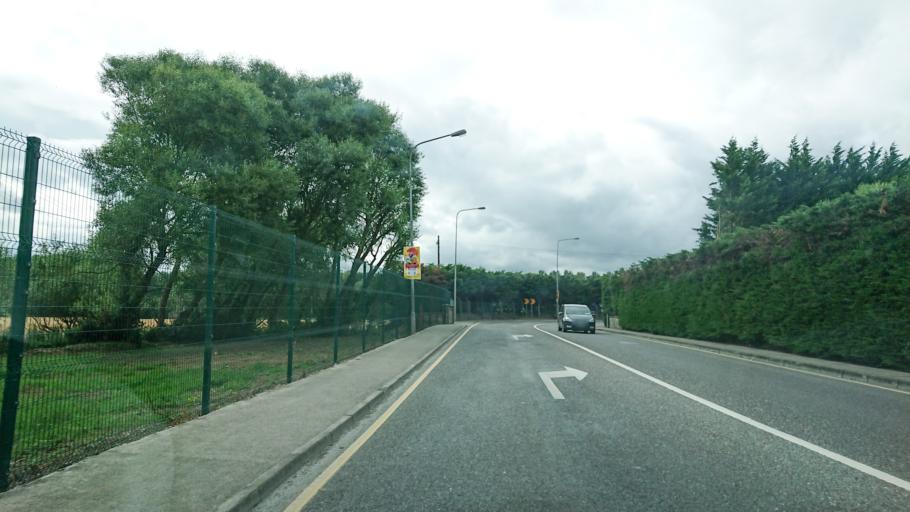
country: IE
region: Munster
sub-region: County Cork
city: Mallow
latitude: 52.1356
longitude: -8.6487
